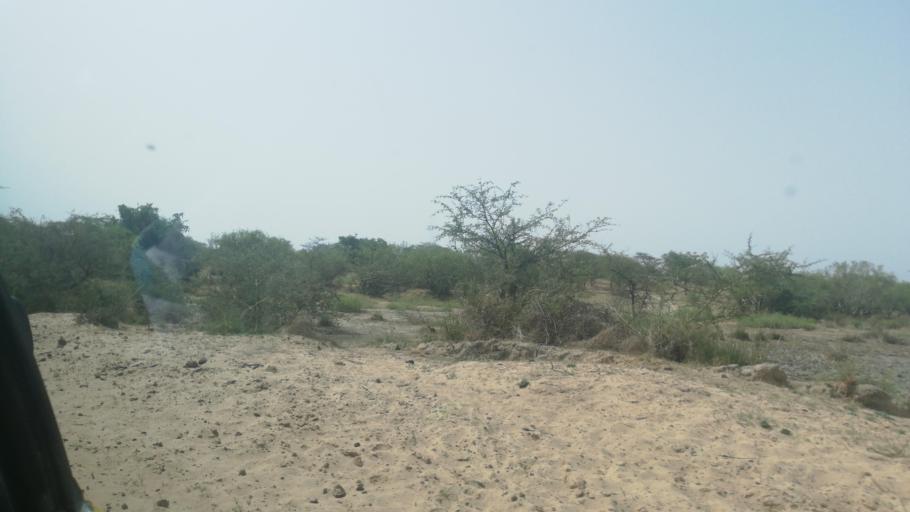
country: SN
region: Saint-Louis
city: Saint-Louis
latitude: 16.0526
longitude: -16.3370
